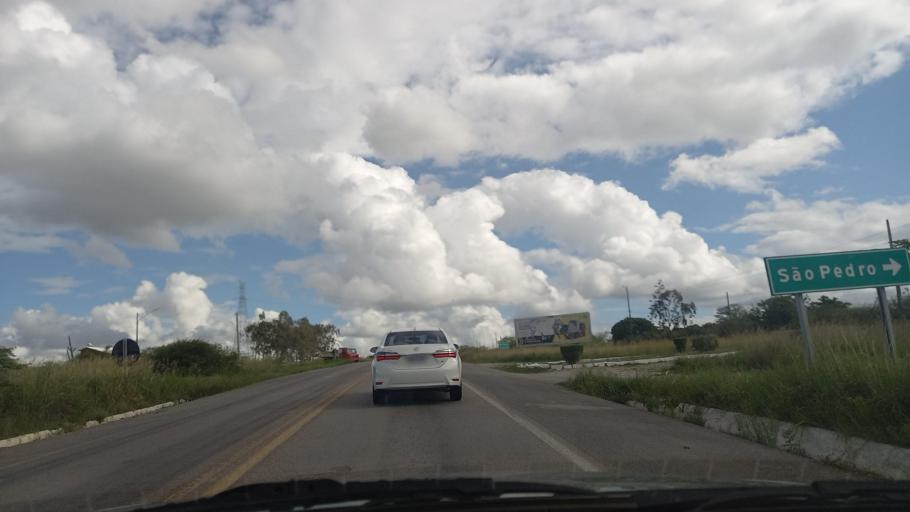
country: BR
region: Pernambuco
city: Garanhuns
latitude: -8.8311
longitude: -36.4531
